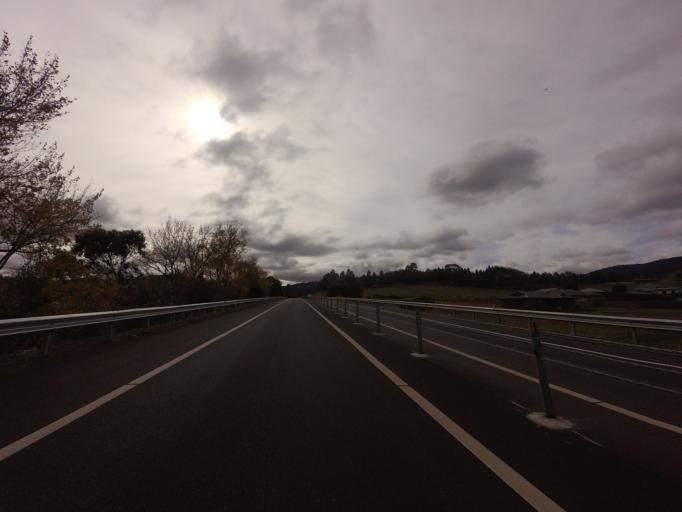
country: AU
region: Tasmania
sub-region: Brighton
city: Bridgewater
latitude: -42.5995
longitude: 147.2202
